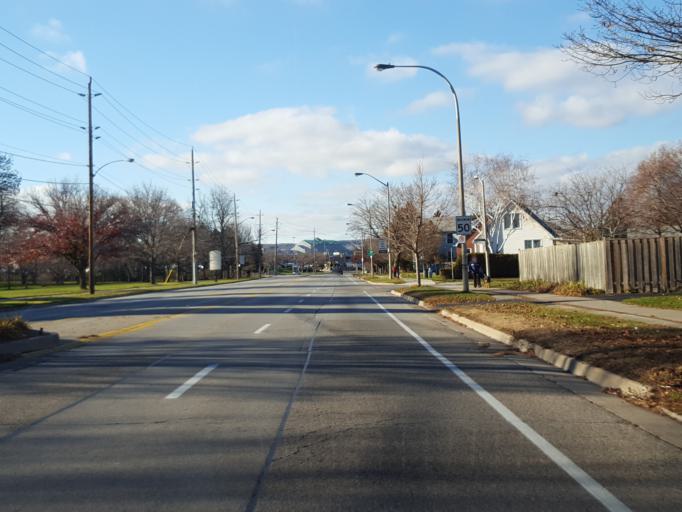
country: CA
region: Ontario
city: Burlington
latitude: 43.3240
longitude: -79.8142
